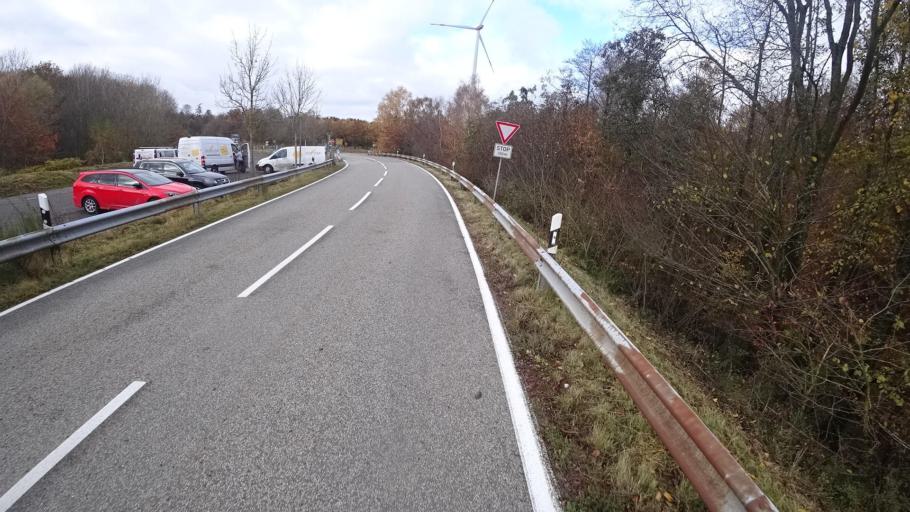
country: DE
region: Rheinland-Pfalz
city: Birkheim
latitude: 50.1188
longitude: 7.6047
